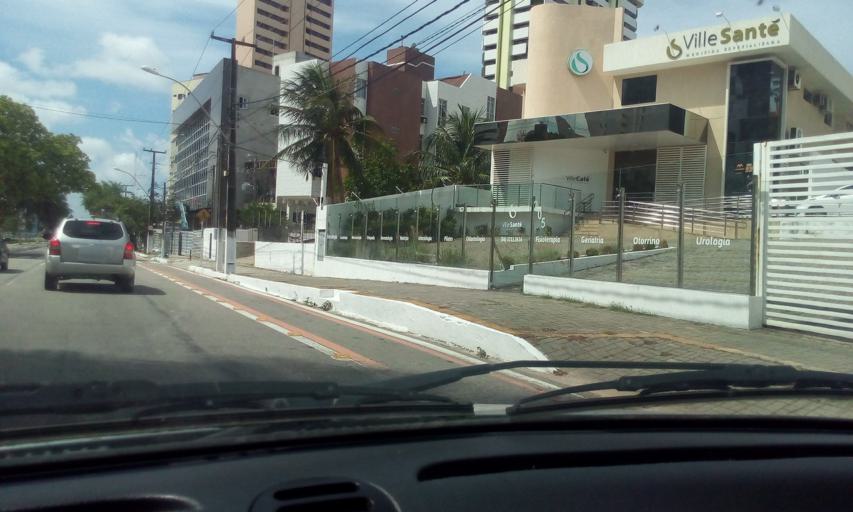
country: BR
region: Rio Grande do Norte
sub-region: Natal
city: Natal
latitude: -5.7947
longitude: -35.2054
